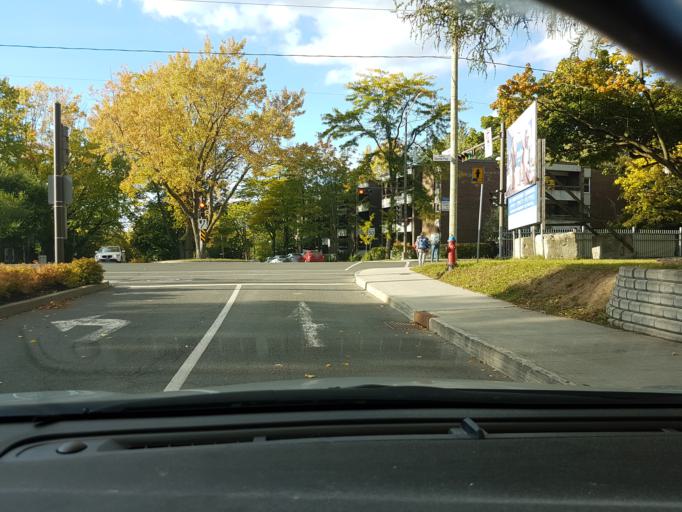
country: CA
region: Quebec
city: Quebec
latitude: 46.7920
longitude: -71.2596
